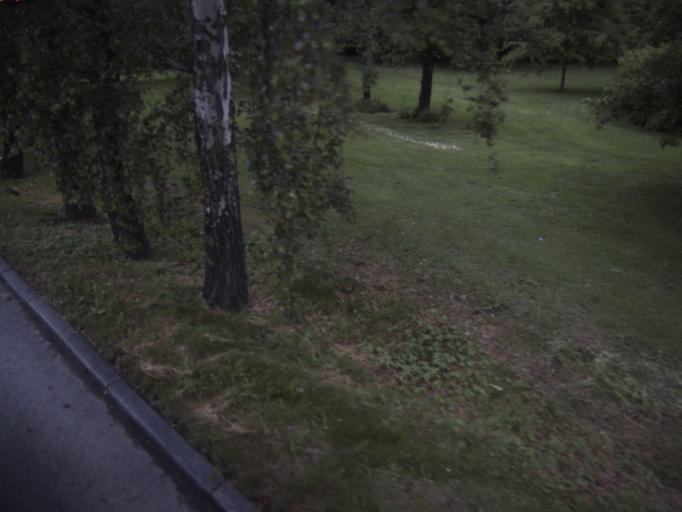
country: SE
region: Skane
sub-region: Helsingborg
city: Rydeback
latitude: 56.0207
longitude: 12.7489
